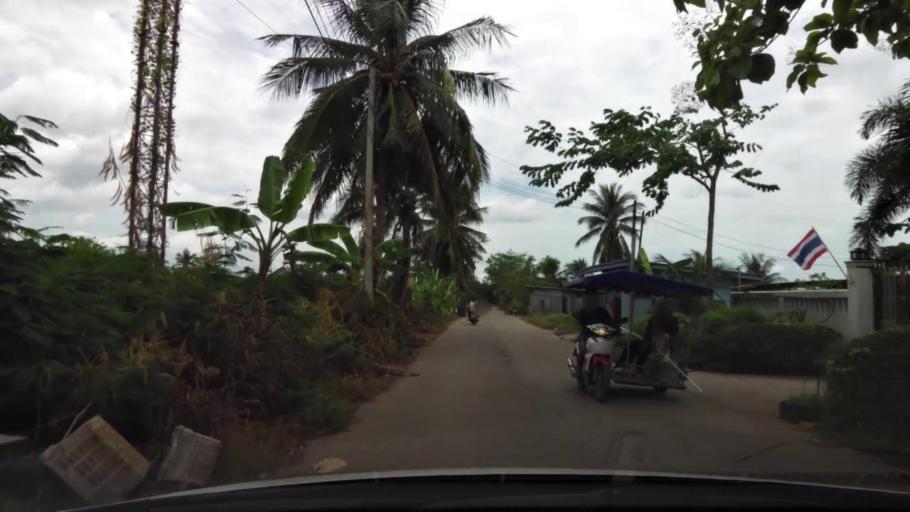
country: TH
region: Samut Sakhon
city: Ban Phaeo
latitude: 13.5593
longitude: 100.0421
